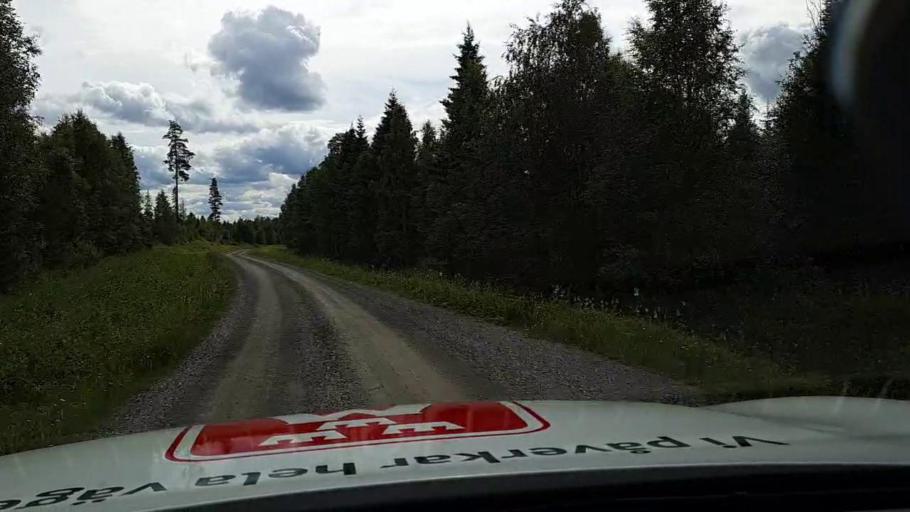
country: SE
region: Jaemtland
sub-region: OEstersunds Kommun
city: Lit
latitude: 63.3043
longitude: 15.2469
